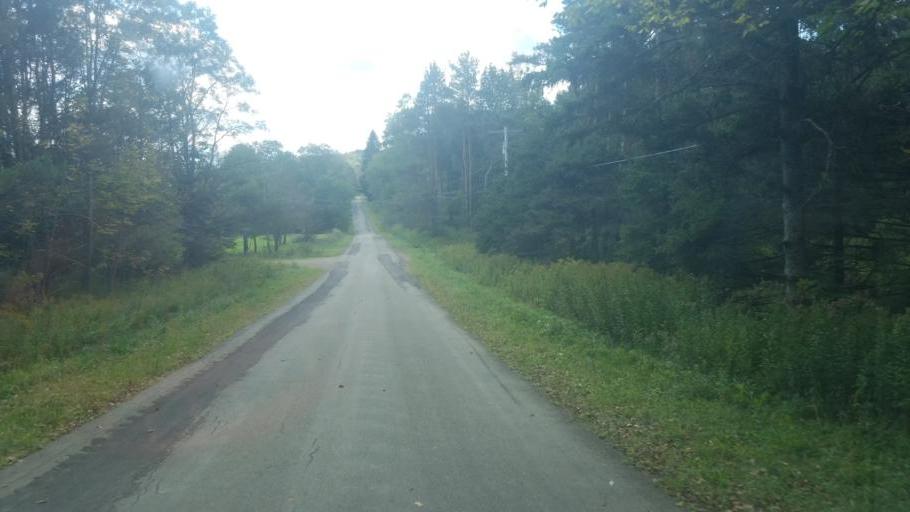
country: US
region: New York
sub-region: Cattaraugus County
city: Franklinville
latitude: 42.2175
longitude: -78.4146
